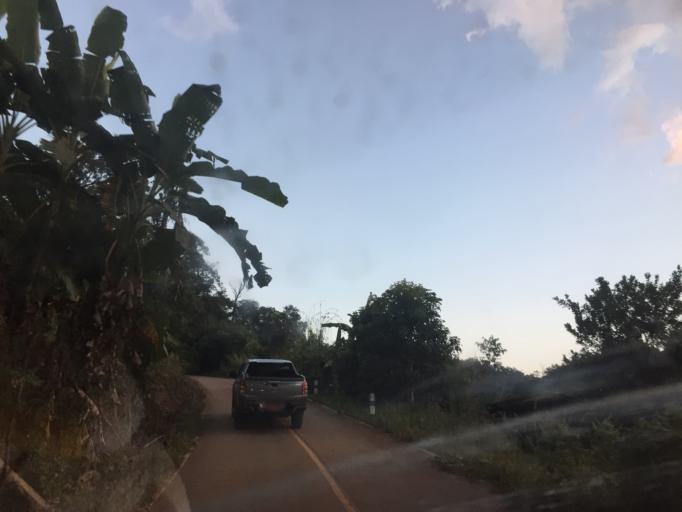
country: TH
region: Chiang Mai
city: Samoeng
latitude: 19.0060
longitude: 98.7099
